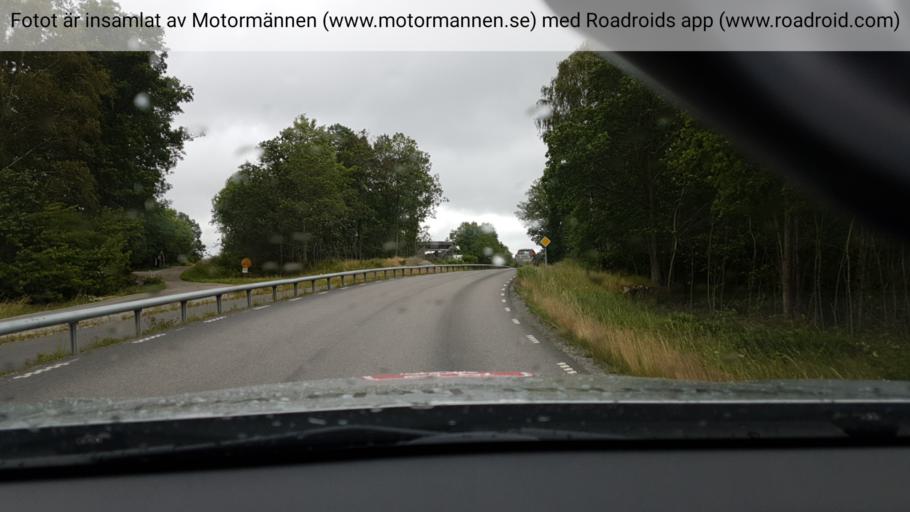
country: SE
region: Vaestra Goetaland
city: Svanesund
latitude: 58.1221
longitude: 11.8559
